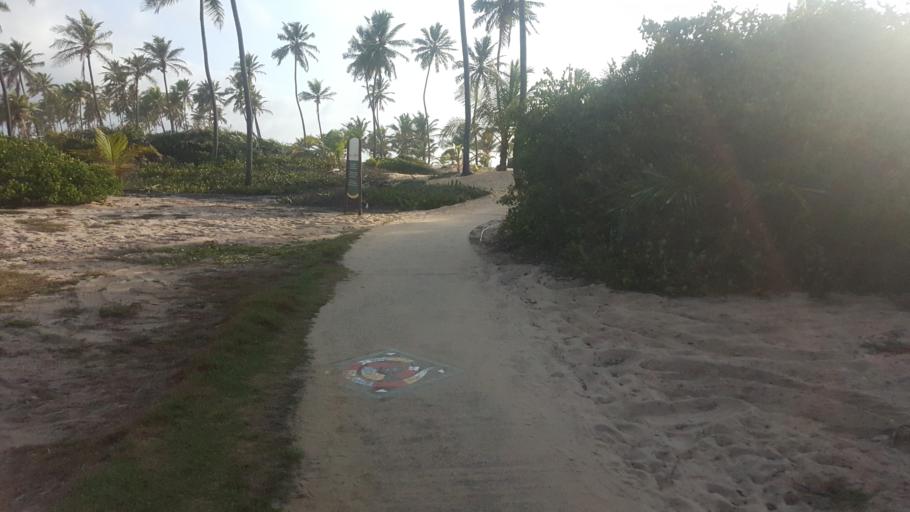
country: BR
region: Bahia
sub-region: Mata De Sao Joao
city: Mata de Sao Joao
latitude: -12.4386
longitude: -37.9165
